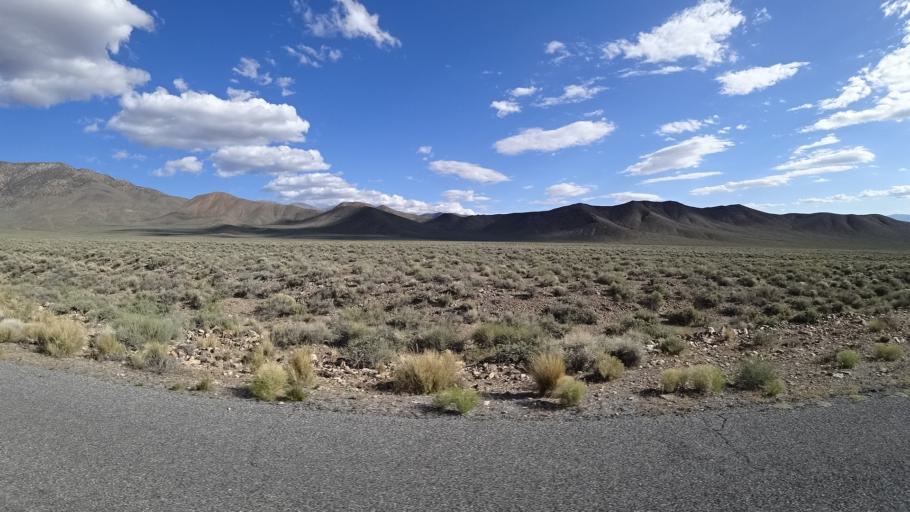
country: US
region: California
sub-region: San Bernardino County
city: Searles Valley
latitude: 36.3061
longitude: -117.1532
